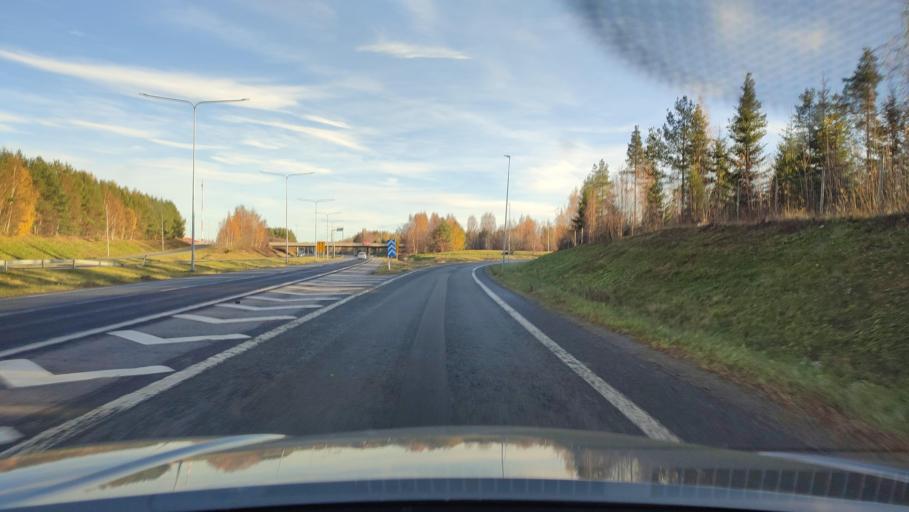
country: FI
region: Ostrobothnia
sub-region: Vaasa
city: Ristinummi
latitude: 63.0305
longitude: 21.7507
